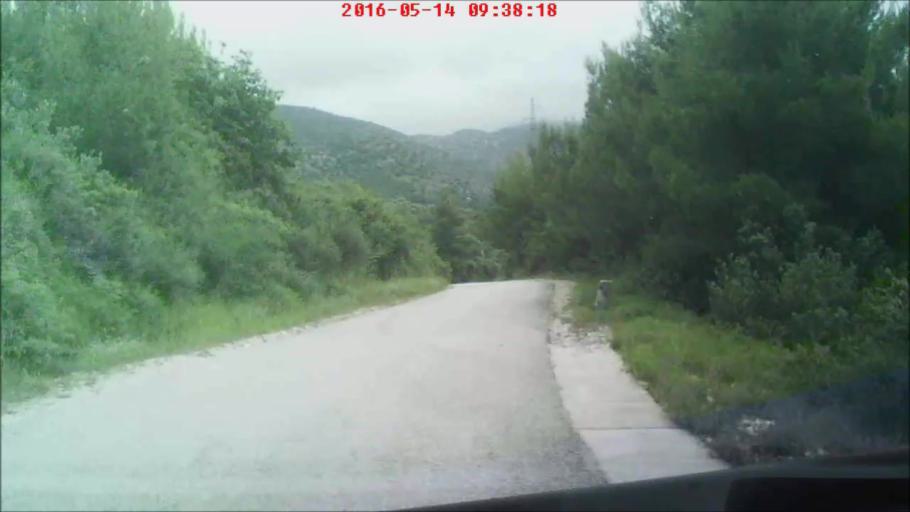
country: HR
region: Dubrovacko-Neretvanska
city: Podgora
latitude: 42.7915
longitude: 17.8870
